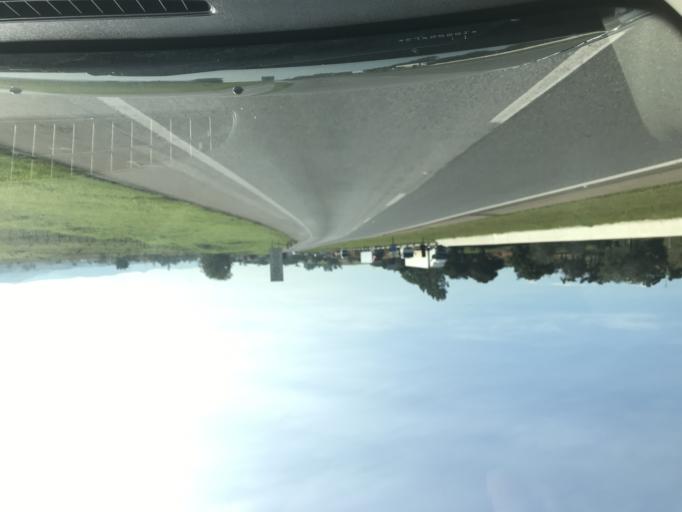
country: BR
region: Minas Gerais
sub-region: Santa Rita Do Sapucai
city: Santa Rita do Sapucai
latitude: -22.1204
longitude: -45.7629
